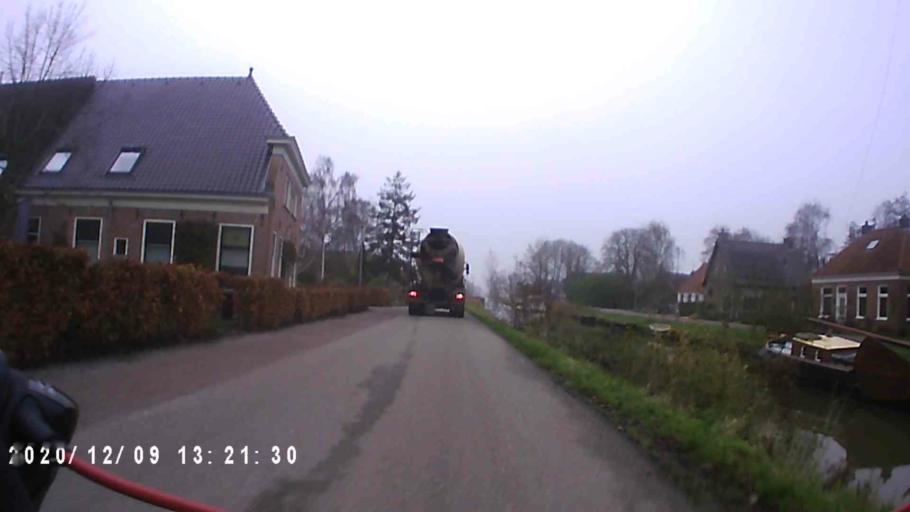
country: NL
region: Groningen
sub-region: Gemeente Groningen
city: Oosterpark
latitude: 53.2615
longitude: 6.5936
